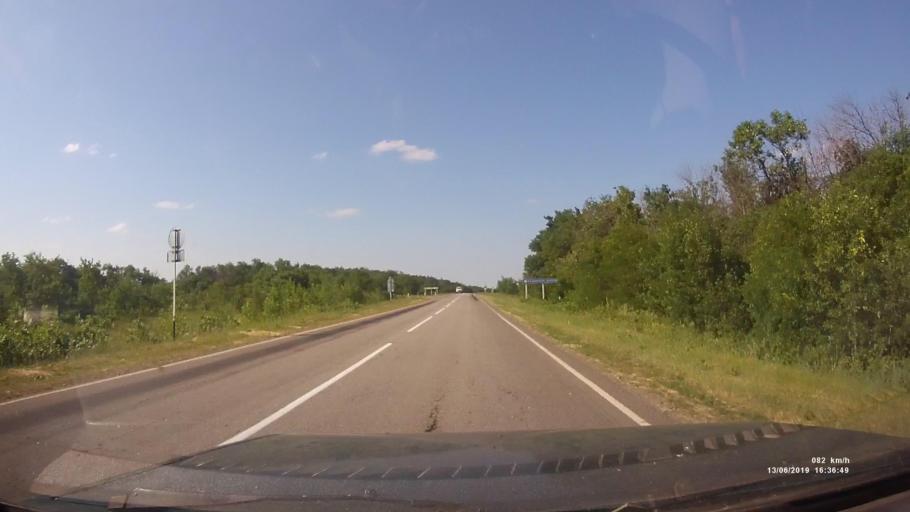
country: RU
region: Rostov
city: Kazanskaya
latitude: 49.8996
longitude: 41.3085
